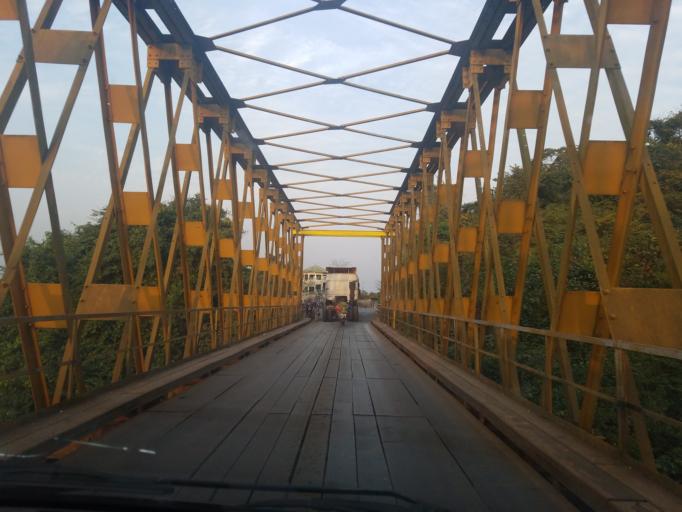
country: GN
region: Boke
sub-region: Fria
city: Fria
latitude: 10.0854
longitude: -13.6777
